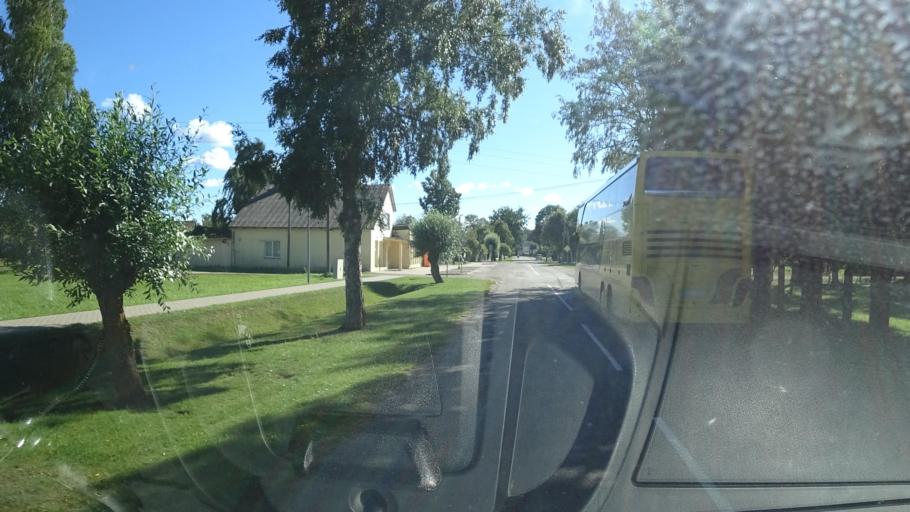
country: LV
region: Dundaga
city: Dundaga
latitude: 57.7443
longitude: 22.5870
